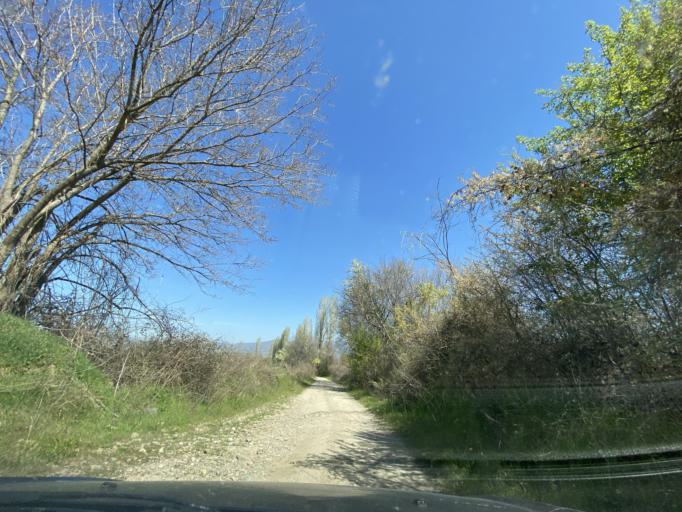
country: MK
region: Zrnovci
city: Zrnovci
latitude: 41.8556
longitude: 22.3891
